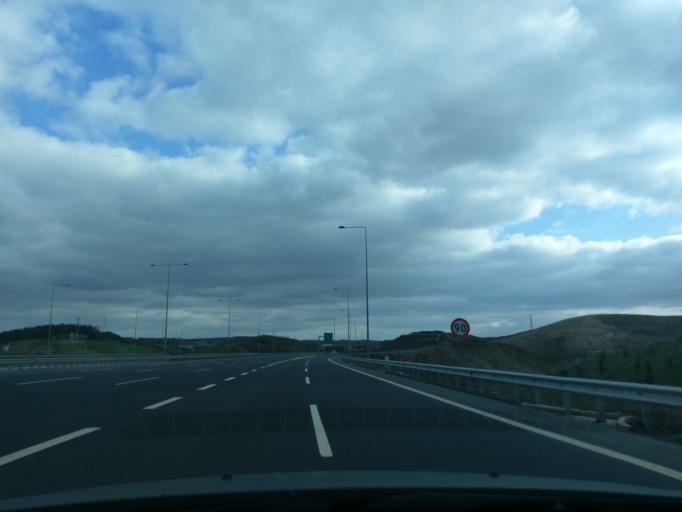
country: TR
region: Istanbul
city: Kemerburgaz
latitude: 41.2368
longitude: 28.8343
